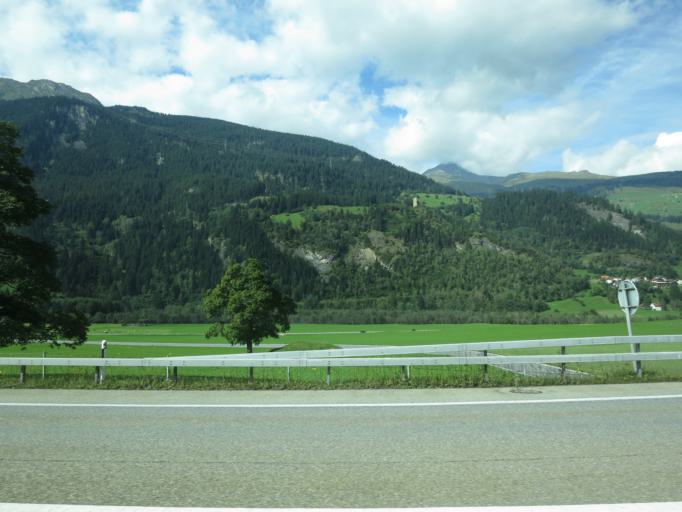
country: CH
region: Grisons
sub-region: Hinterrhein District
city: Thusis
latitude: 46.6082
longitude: 9.4334
